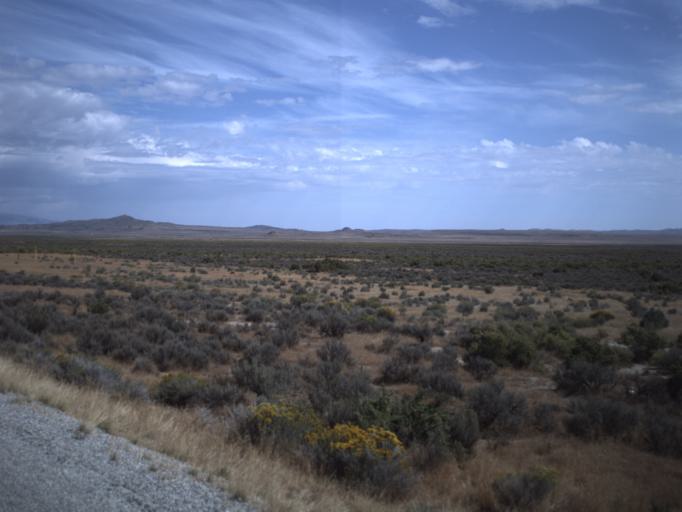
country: US
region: Utah
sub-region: Tooele County
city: Wendover
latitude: 41.5667
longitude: -113.5811
